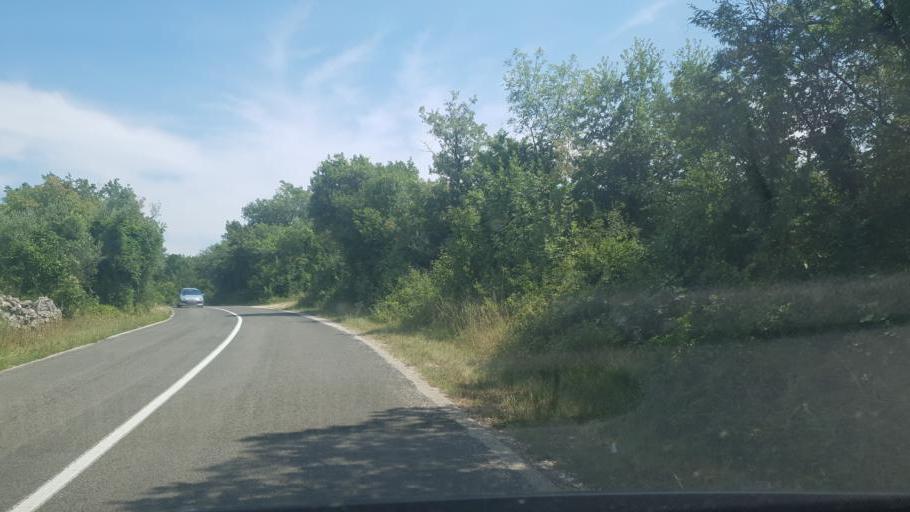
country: HR
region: Primorsko-Goranska
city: Njivice
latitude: 45.1430
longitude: 14.6124
